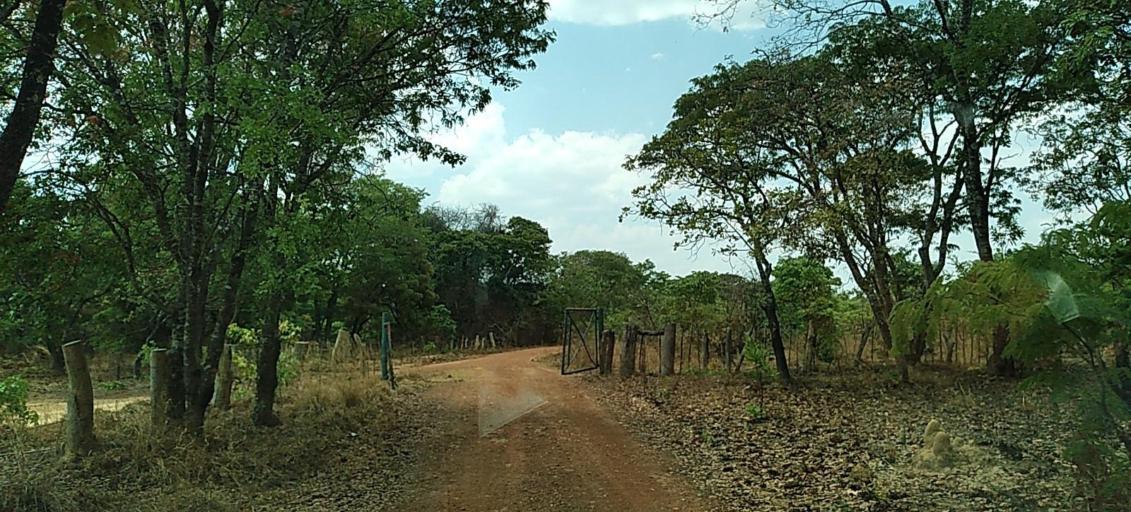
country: ZM
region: Copperbelt
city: Chililabombwe
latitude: -12.4591
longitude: 27.6454
